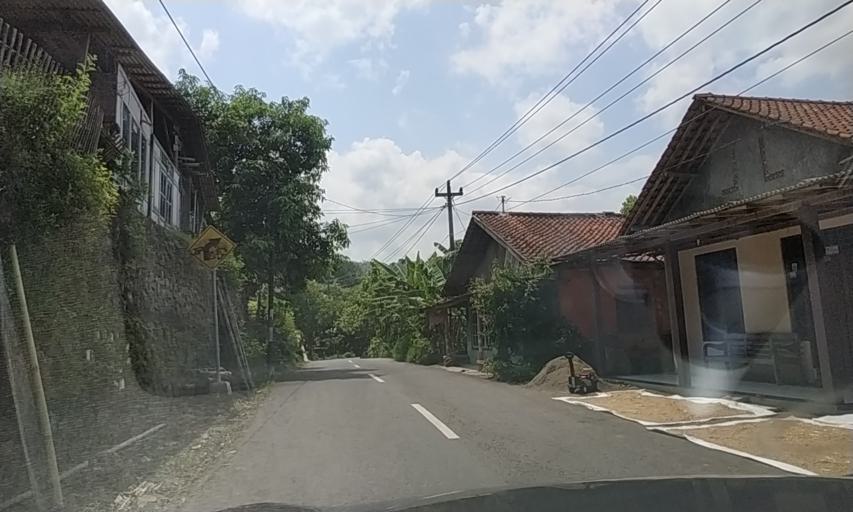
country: ID
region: Central Java
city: Gombong
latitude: -7.6253
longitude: 109.7232
